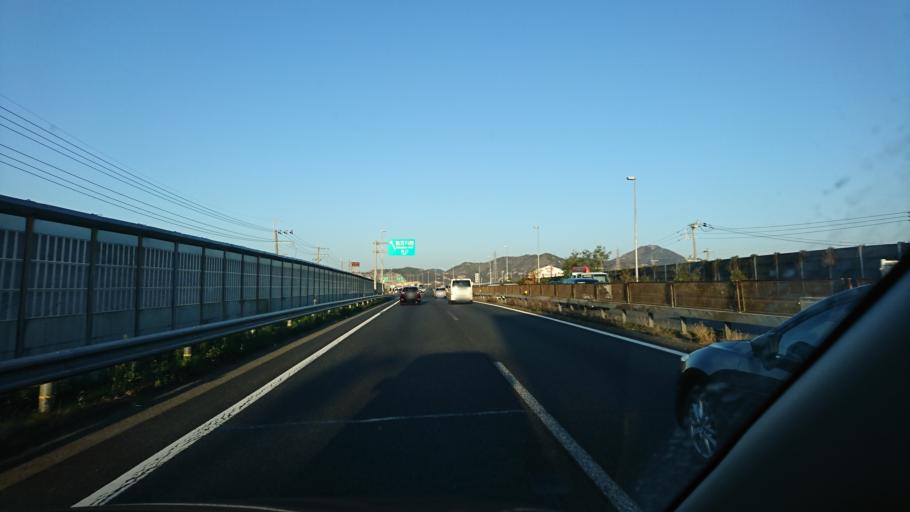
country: JP
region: Hyogo
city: Kakogawacho-honmachi
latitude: 34.7860
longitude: 134.8239
